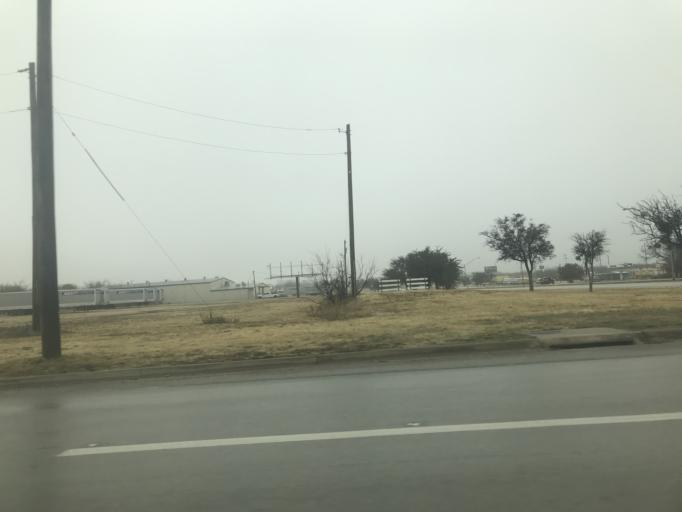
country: US
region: Texas
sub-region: Taylor County
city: Tye
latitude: 32.4434
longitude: -99.8093
